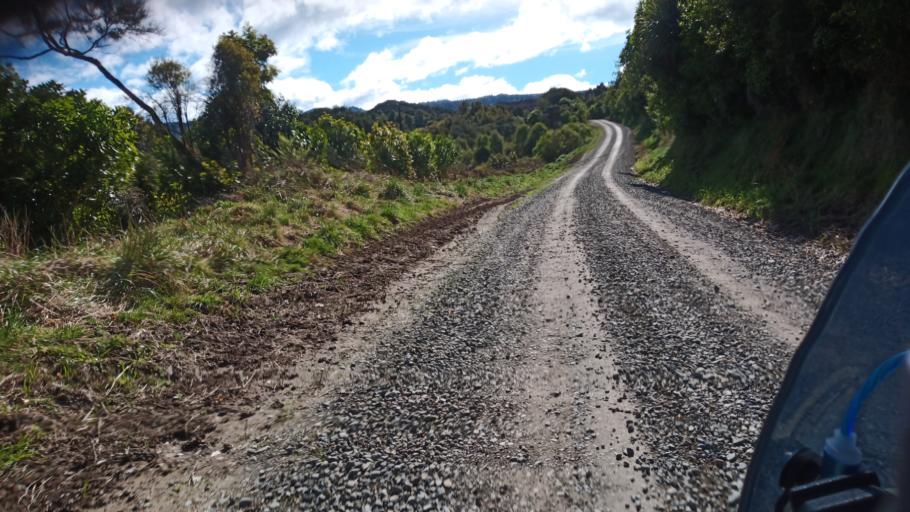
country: NZ
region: Hawke's Bay
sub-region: Wairoa District
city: Wairoa
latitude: -38.8227
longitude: 177.1624
